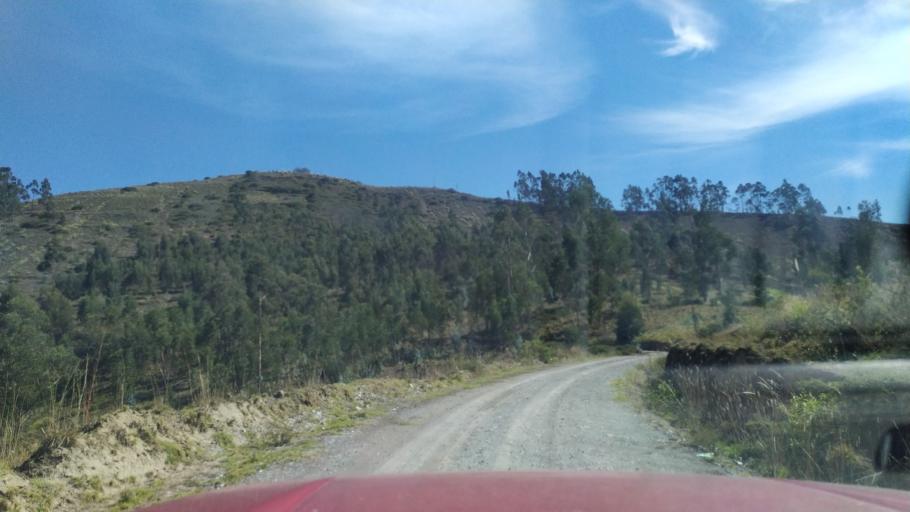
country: EC
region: Chimborazo
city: Riobamba
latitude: -1.6770
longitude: -78.6951
